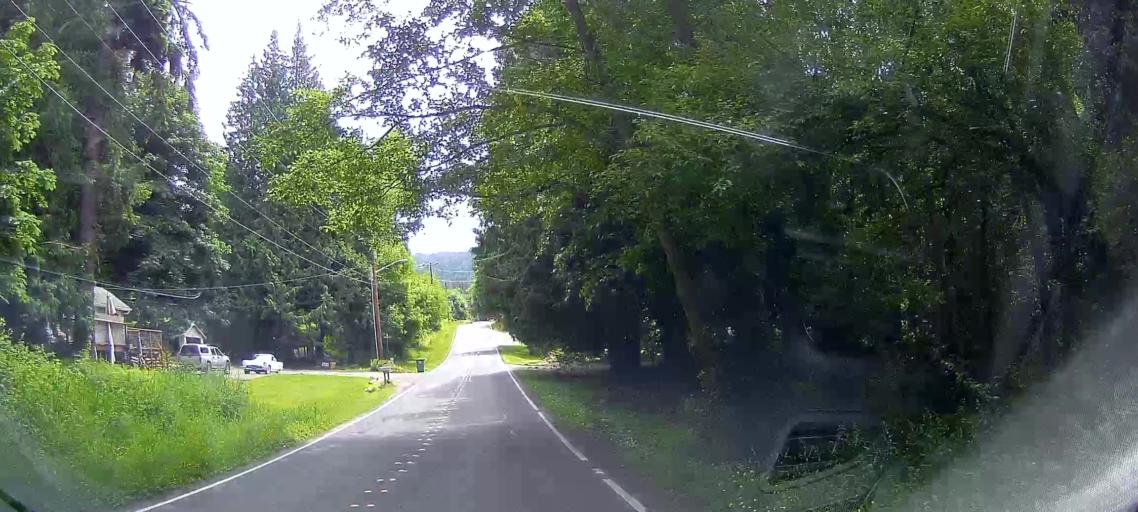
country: US
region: Washington
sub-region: Whatcom County
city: Bellingham
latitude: 48.7105
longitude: -122.4783
